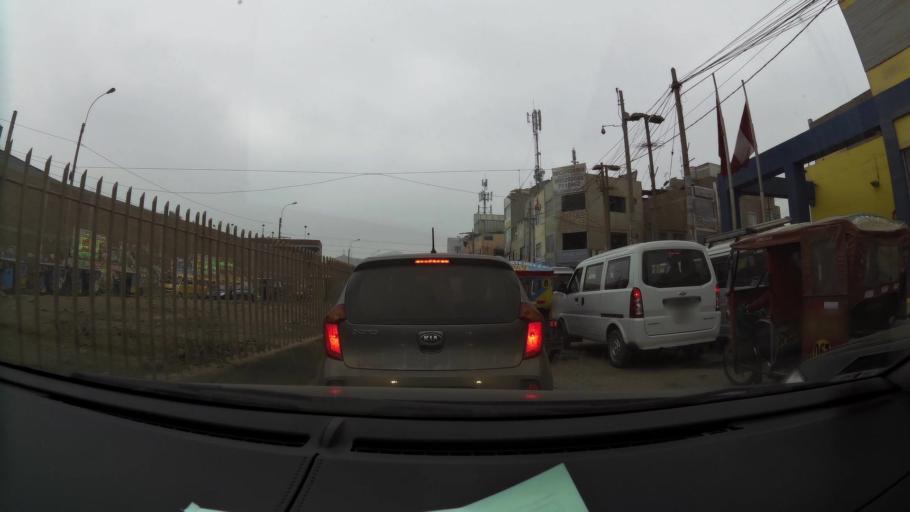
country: PE
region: Lima
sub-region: Lima
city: Carabayllo
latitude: -11.8643
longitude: -77.0731
